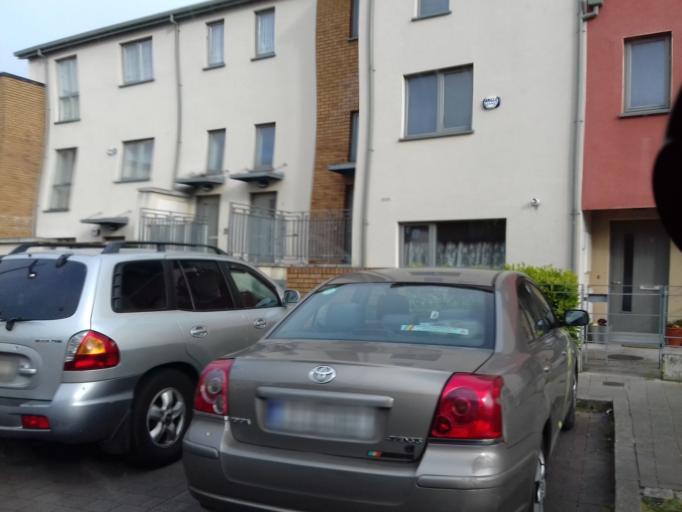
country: IE
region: Leinster
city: Ballymun
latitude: 53.3929
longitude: -6.2703
